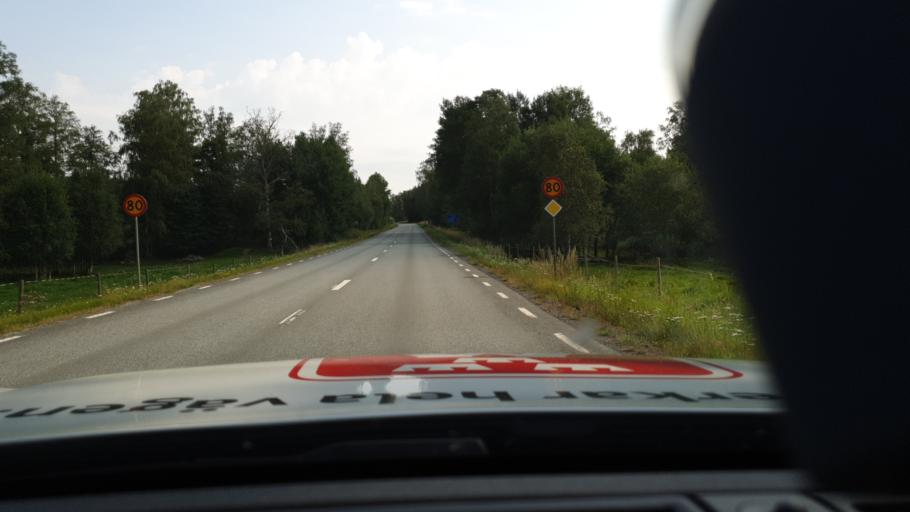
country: SE
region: Joenkoeping
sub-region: Jonkopings Kommun
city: Tenhult
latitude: 57.7757
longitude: 14.4289
